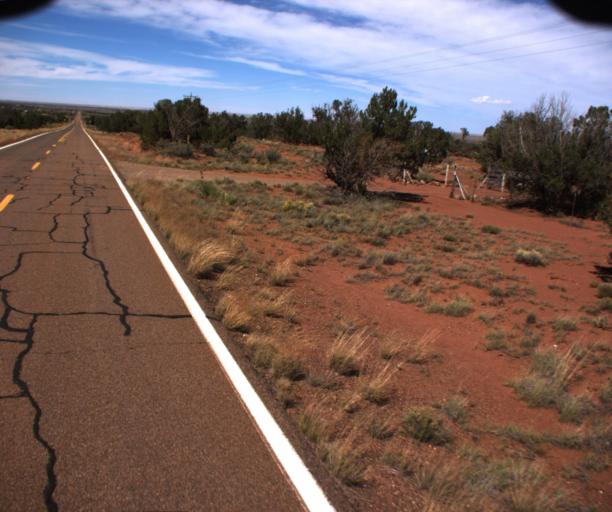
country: US
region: Arizona
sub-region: Apache County
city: Saint Johns
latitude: 34.5877
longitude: -109.6446
